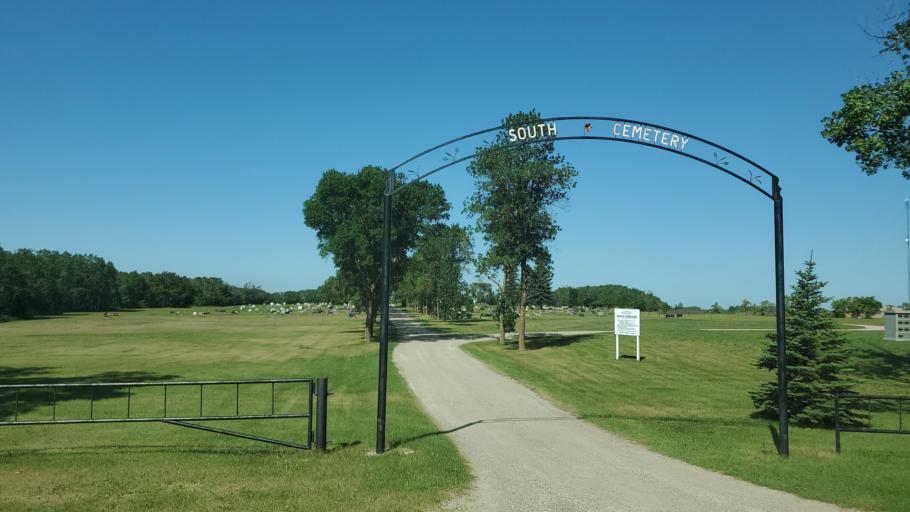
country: CA
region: Saskatchewan
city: Moosomin
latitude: 50.1340
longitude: -101.6769
